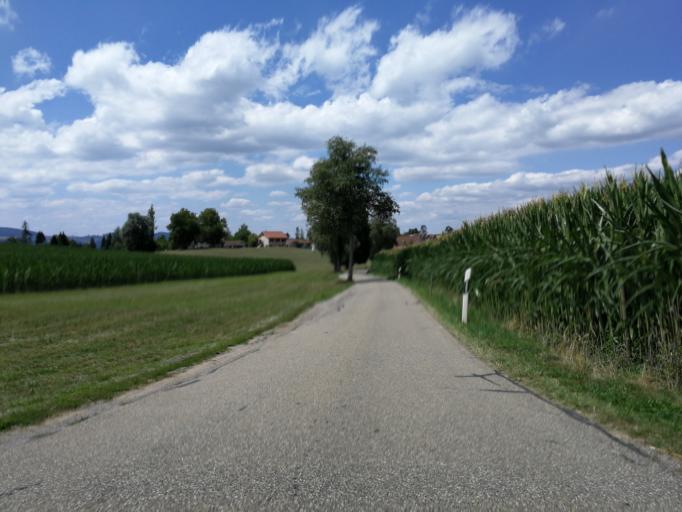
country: CH
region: Zurich
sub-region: Bezirk Hinwil
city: Gossau
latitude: 47.3172
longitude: 8.7615
